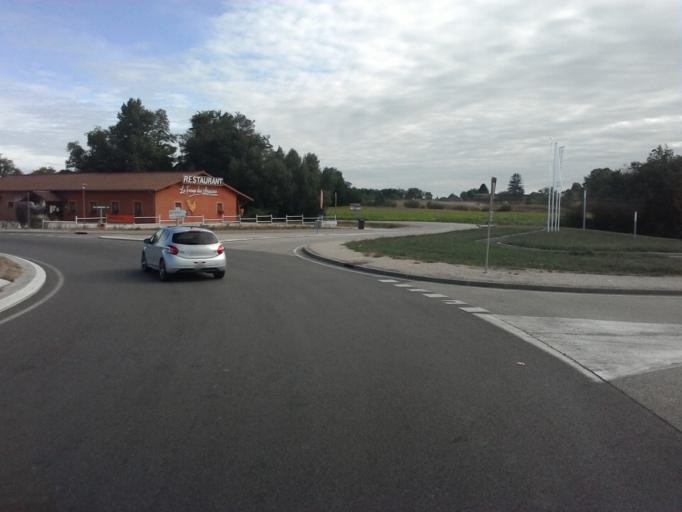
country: FR
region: Rhone-Alpes
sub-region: Departement de l'Ain
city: Montagnat
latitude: 46.1555
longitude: 5.2748
